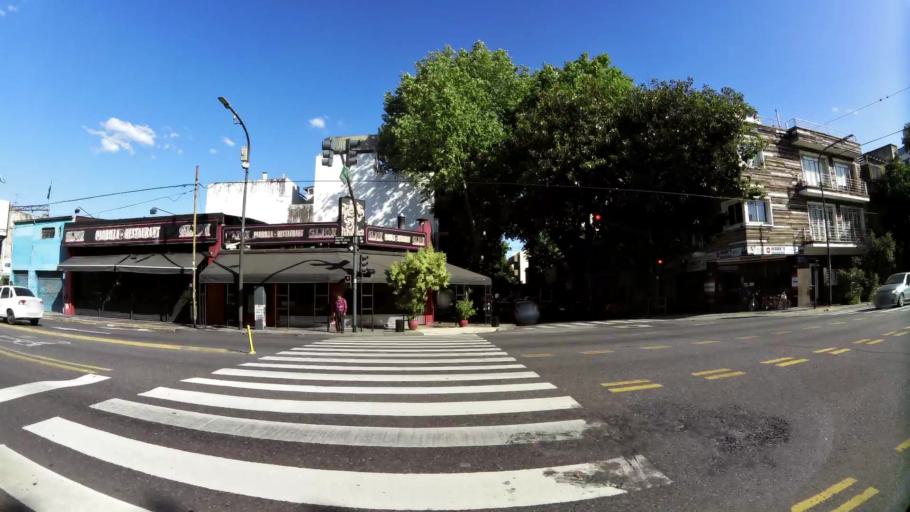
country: AR
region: Buenos Aires F.D.
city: Villa Santa Rita
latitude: -34.6160
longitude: -58.4741
